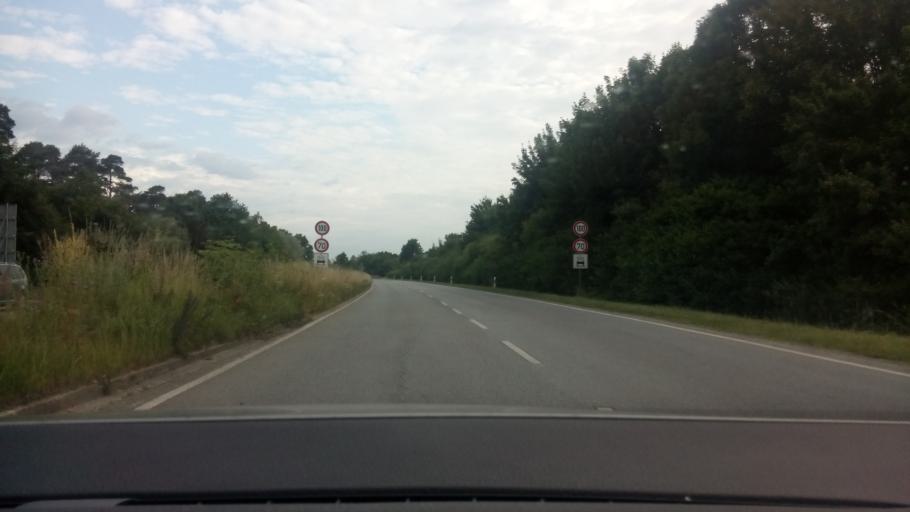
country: DE
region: Bavaria
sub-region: Upper Bavaria
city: Oberschleissheim
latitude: 48.2491
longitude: 11.6021
